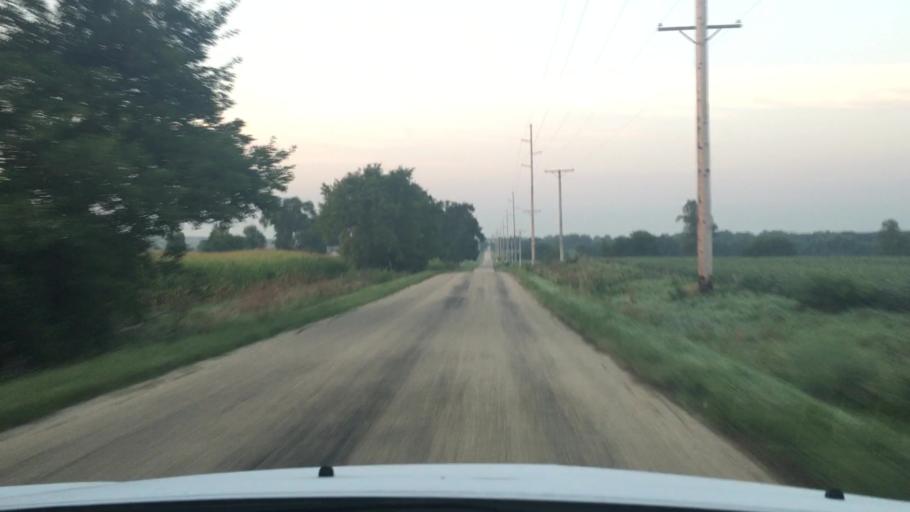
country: US
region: Illinois
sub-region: Ogle County
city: Rochelle
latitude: 41.8536
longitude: -89.0005
